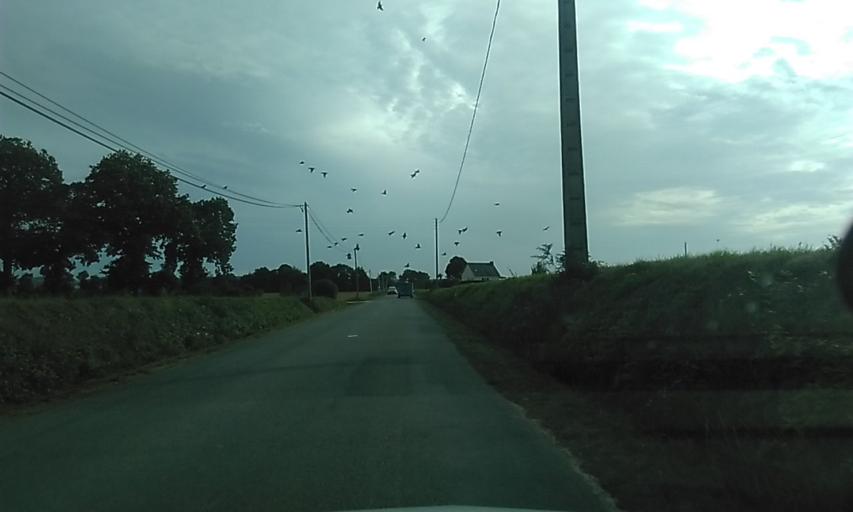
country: FR
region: Brittany
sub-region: Departement d'Ille-et-Vilaine
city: Iffendic
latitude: 48.1430
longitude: -2.0186
